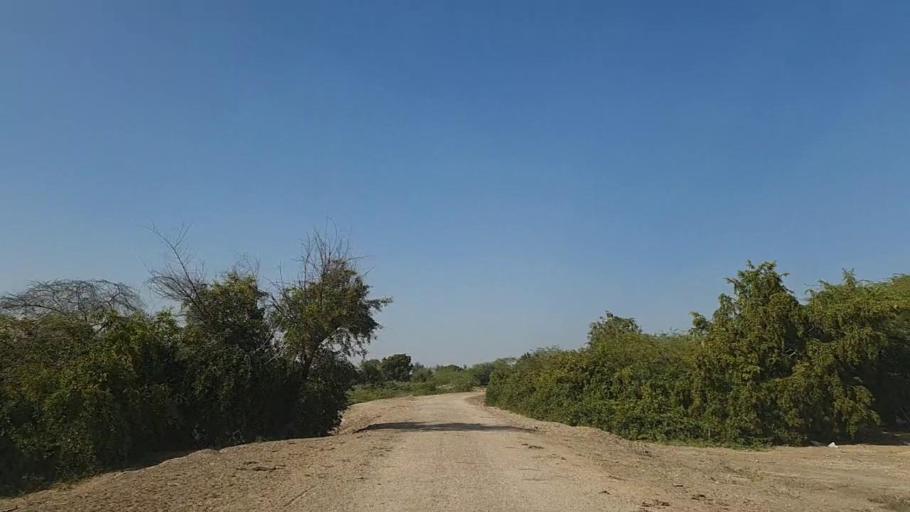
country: PK
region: Sindh
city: Samaro
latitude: 25.3599
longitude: 69.4229
